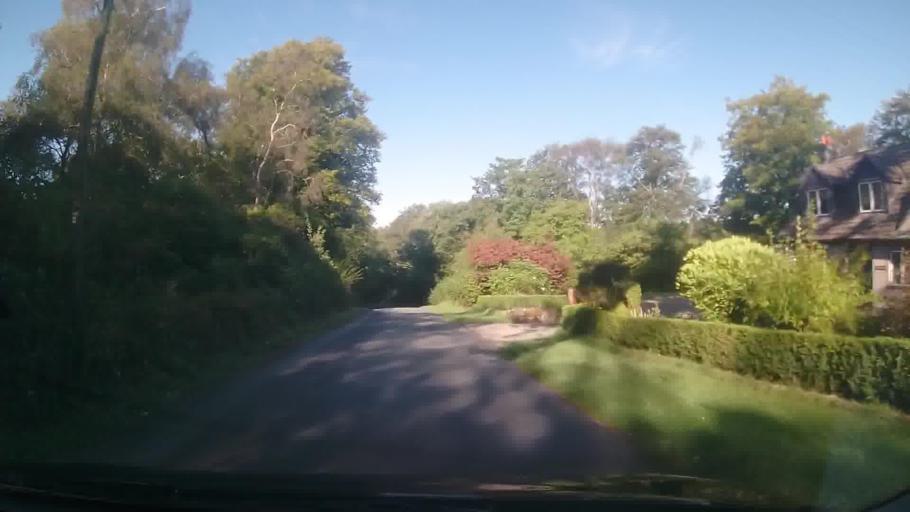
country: GB
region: England
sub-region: Cumbria
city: Seascale
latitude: 54.4001
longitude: -3.3726
